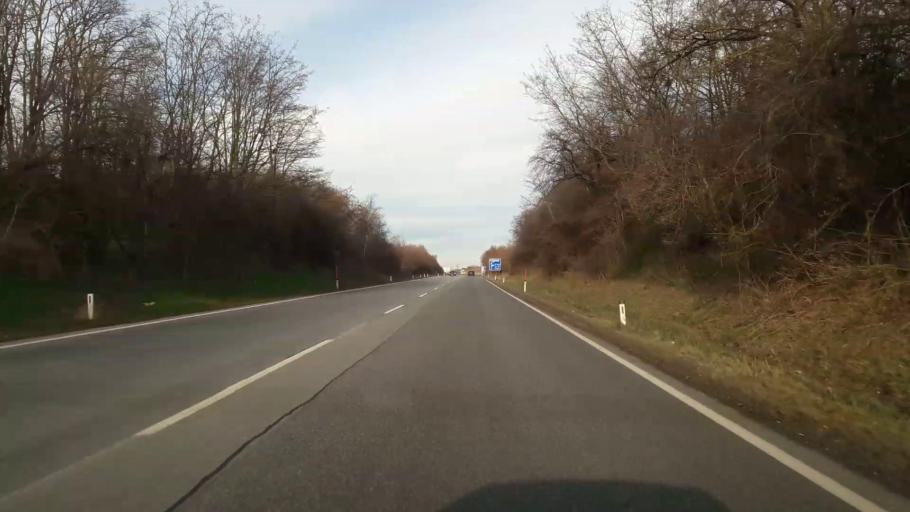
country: AT
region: Lower Austria
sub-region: Politischer Bezirk Mistelbach
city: Gaweinstal
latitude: 48.4896
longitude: 16.5960
